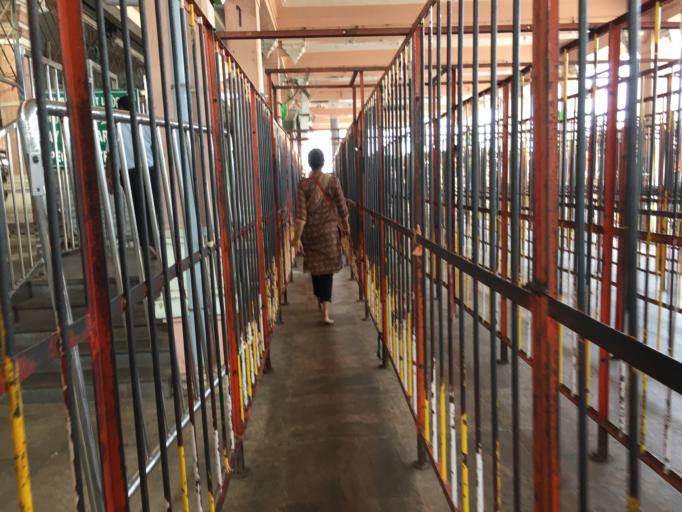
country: IN
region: Tamil Nadu
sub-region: Dindigul
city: Palani
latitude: 10.4388
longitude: 77.5210
